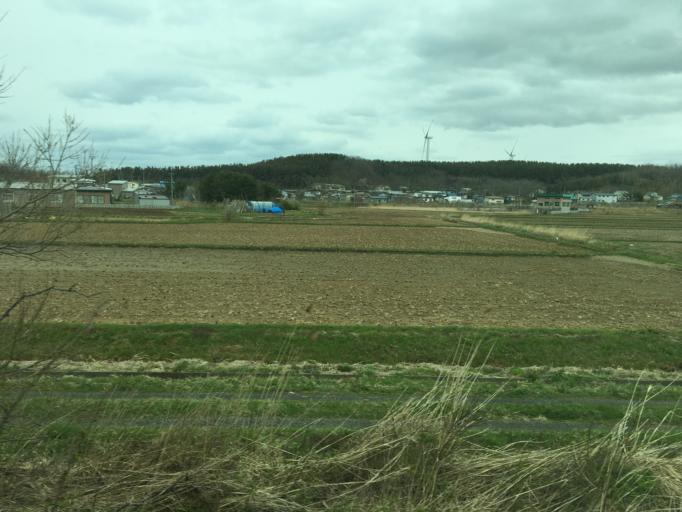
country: JP
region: Aomori
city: Shimokizukuri
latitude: 40.7865
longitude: 140.2432
